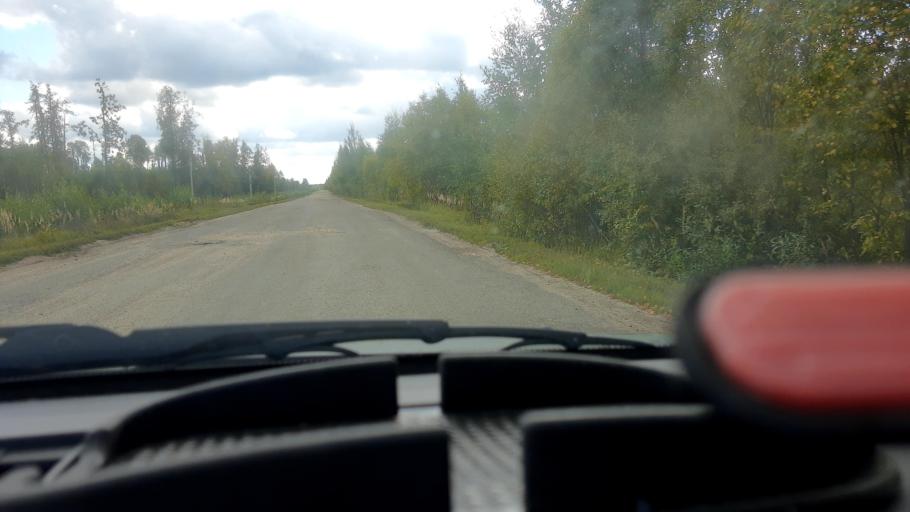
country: RU
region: Mariy-El
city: Kilemary
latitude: 56.8974
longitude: 46.7471
